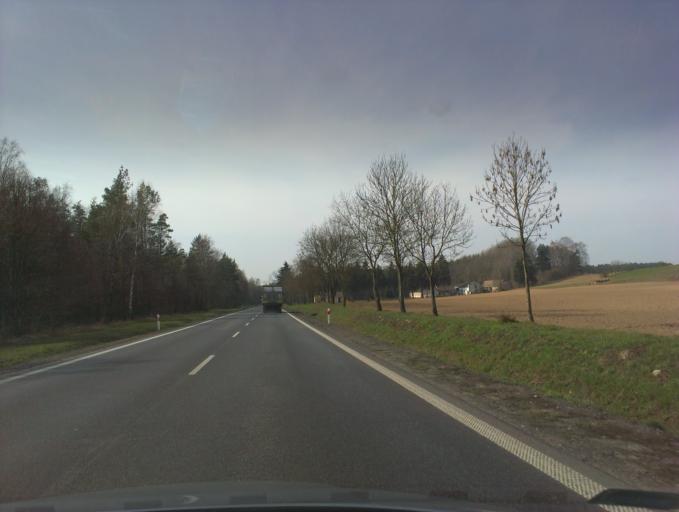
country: PL
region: Greater Poland Voivodeship
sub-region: Powiat zlotowski
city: Jastrowie
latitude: 53.4649
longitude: 16.8629
